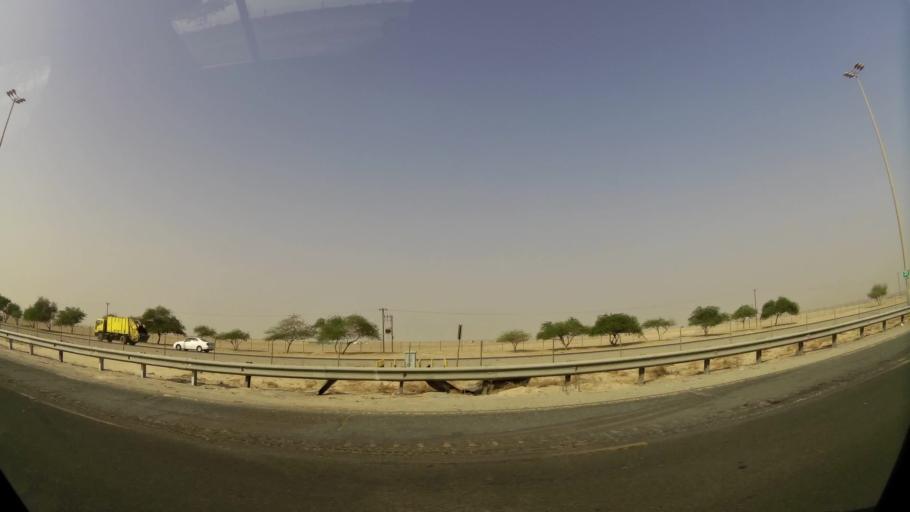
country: KW
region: Al Asimah
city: Ar Rabiyah
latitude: 29.2167
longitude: 47.8849
